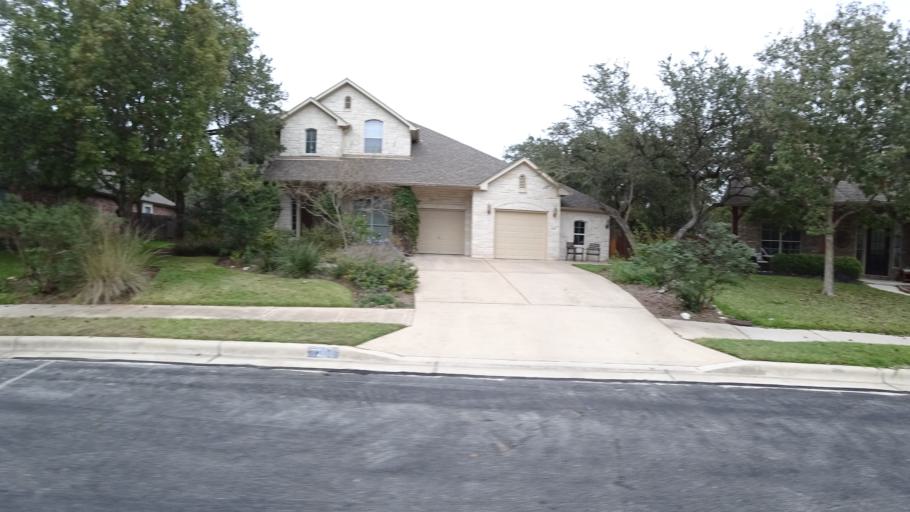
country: US
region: Texas
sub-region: Travis County
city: Shady Hollow
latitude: 30.1897
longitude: -97.9082
